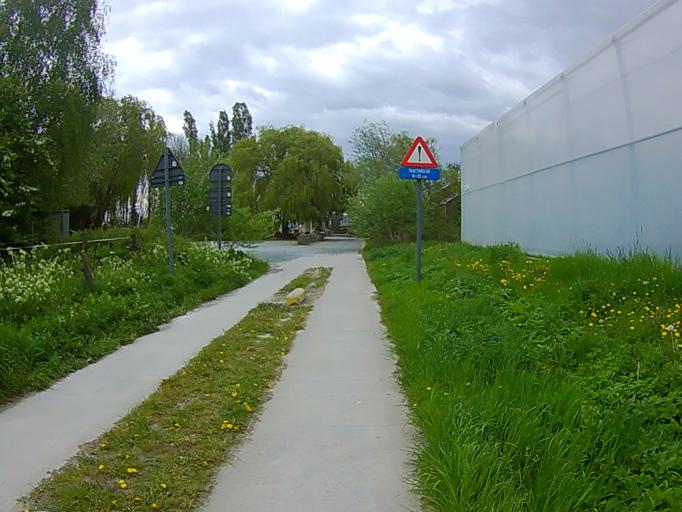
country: BE
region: Flanders
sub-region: Provincie Vlaams-Brabant
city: Merchtem
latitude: 50.9799
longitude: 4.2235
